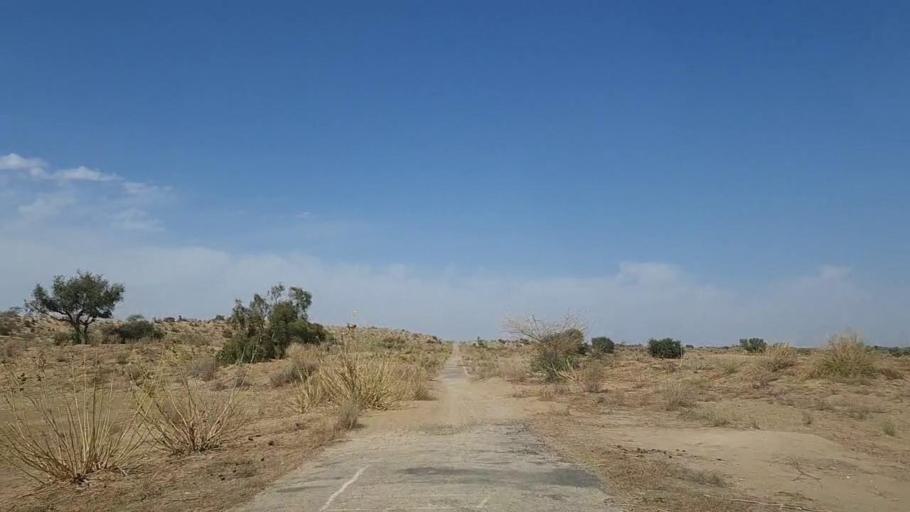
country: PK
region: Sindh
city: Nabisar
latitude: 24.8752
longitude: 69.6109
